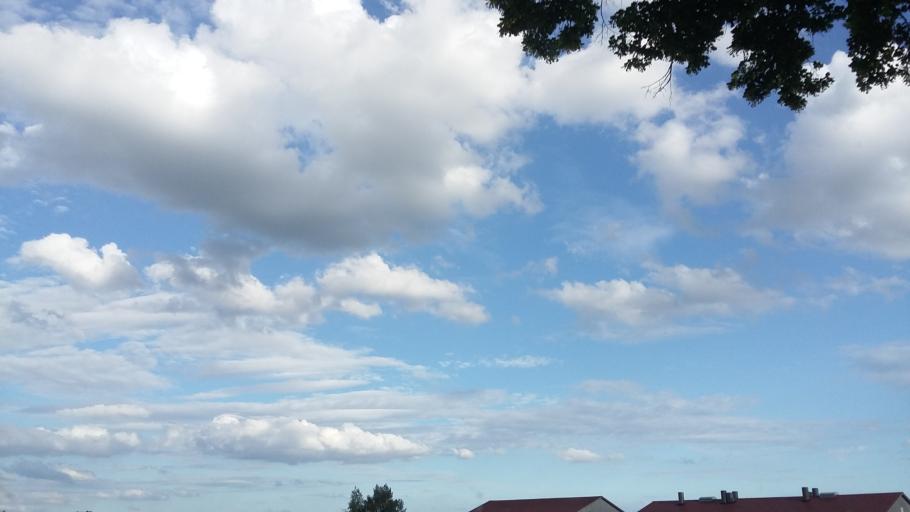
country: DE
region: Bavaria
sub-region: Swabia
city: Steindorf
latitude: 48.2365
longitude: 11.0051
